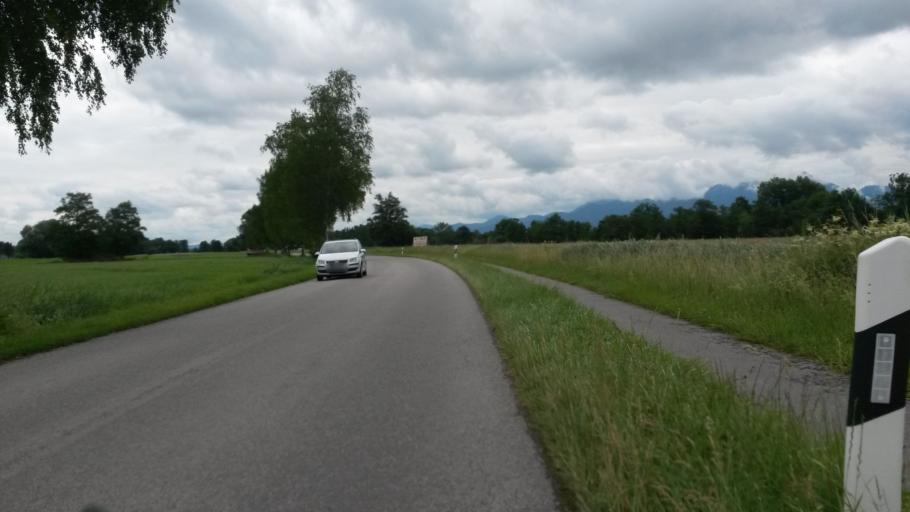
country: DE
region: Bavaria
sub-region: Upper Bavaria
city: Prien am Chiemsee
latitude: 47.8378
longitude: 12.3588
